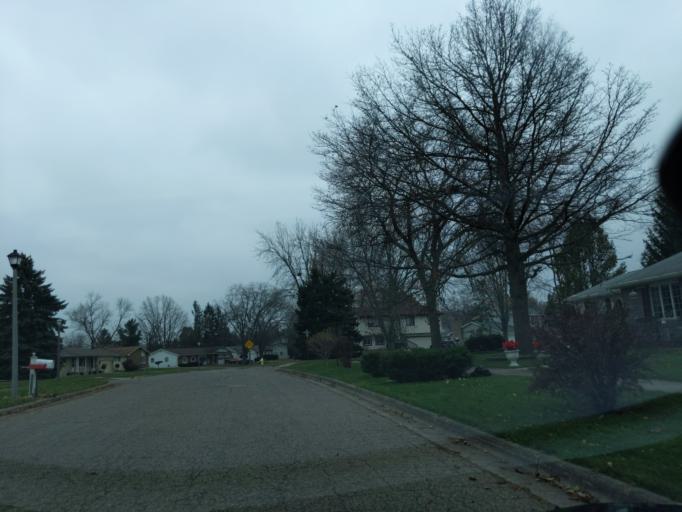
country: US
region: Michigan
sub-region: Eaton County
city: Waverly
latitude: 42.7226
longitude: -84.6290
